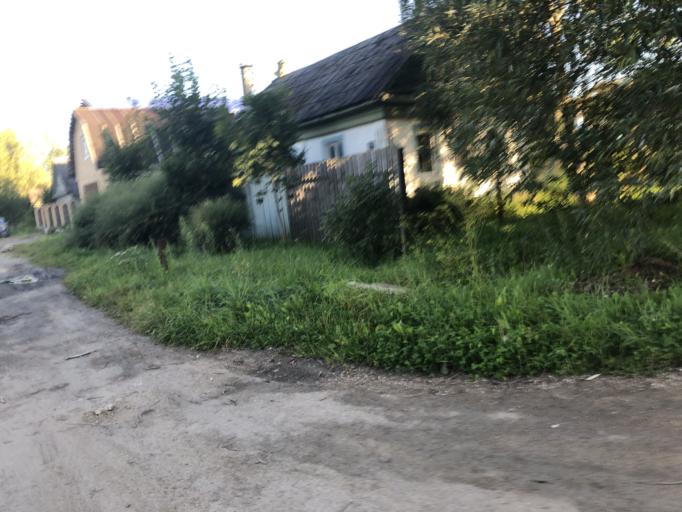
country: RU
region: Tverskaya
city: Rzhev
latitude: 56.2440
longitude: 34.3099
